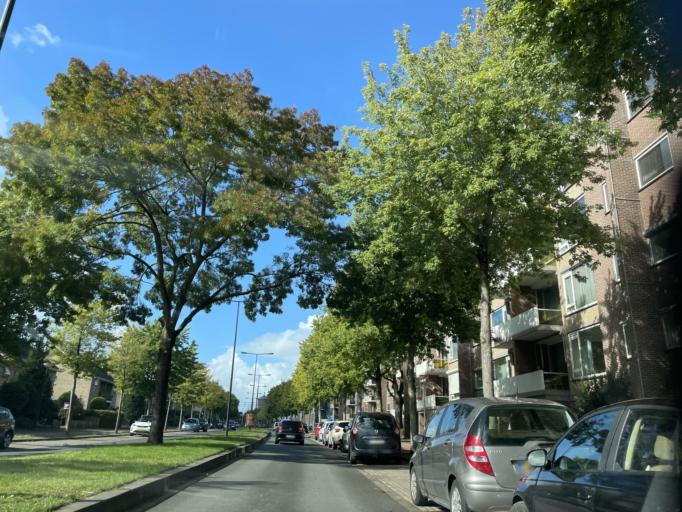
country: NL
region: North Brabant
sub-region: Gemeente Bergen op Zoom
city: Bergen op Zoom
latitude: 51.4894
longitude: 4.3031
